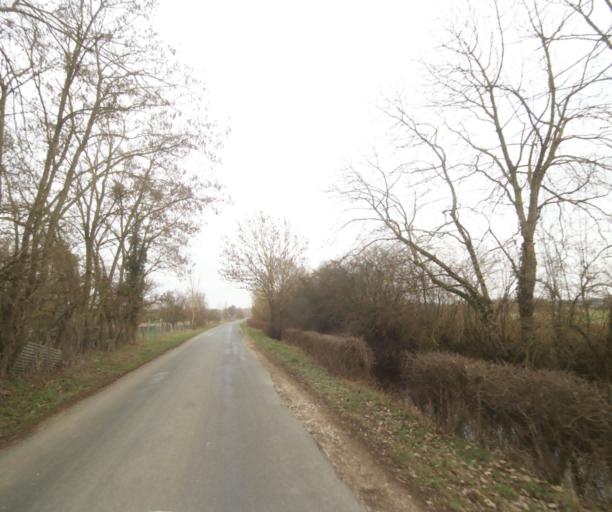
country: FR
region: Champagne-Ardenne
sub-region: Departement de la Haute-Marne
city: Villiers-en-Lieu
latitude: 48.6575
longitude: 4.8270
